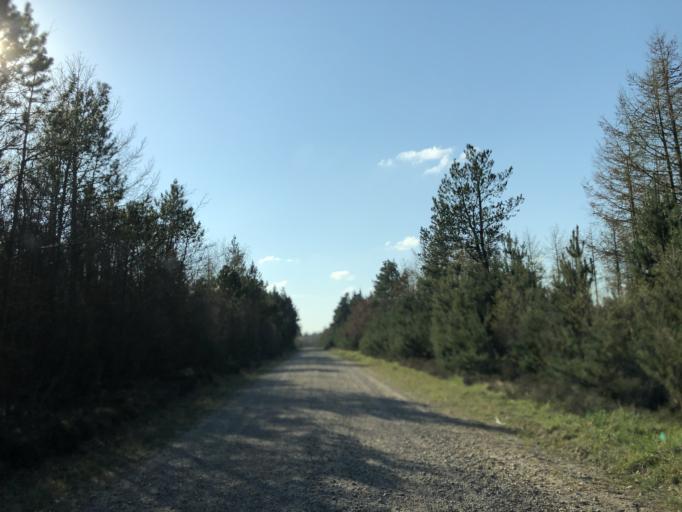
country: DK
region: Central Jutland
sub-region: Holstebro Kommune
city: Ulfborg
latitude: 56.3688
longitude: 8.3048
